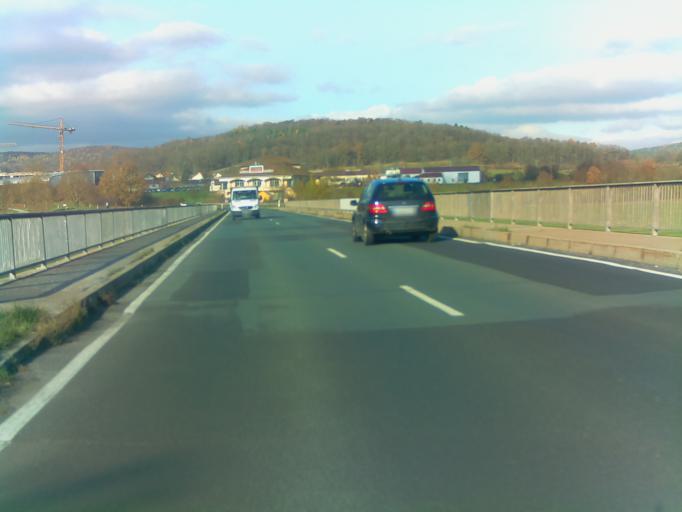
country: DE
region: Bavaria
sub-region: Regierungsbezirk Unterfranken
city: Bad Bocklet
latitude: 50.2411
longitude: 10.0760
